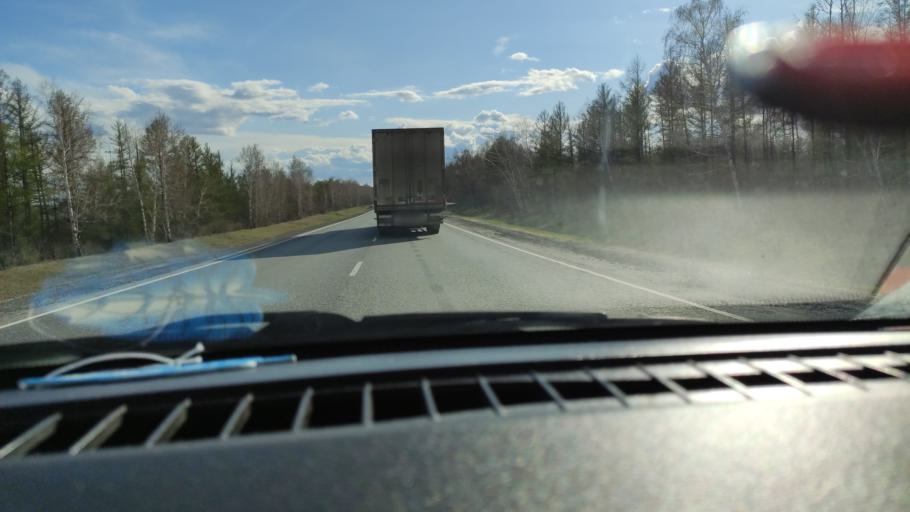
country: RU
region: Saratov
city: Sennoy
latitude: 52.1265
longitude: 46.8547
